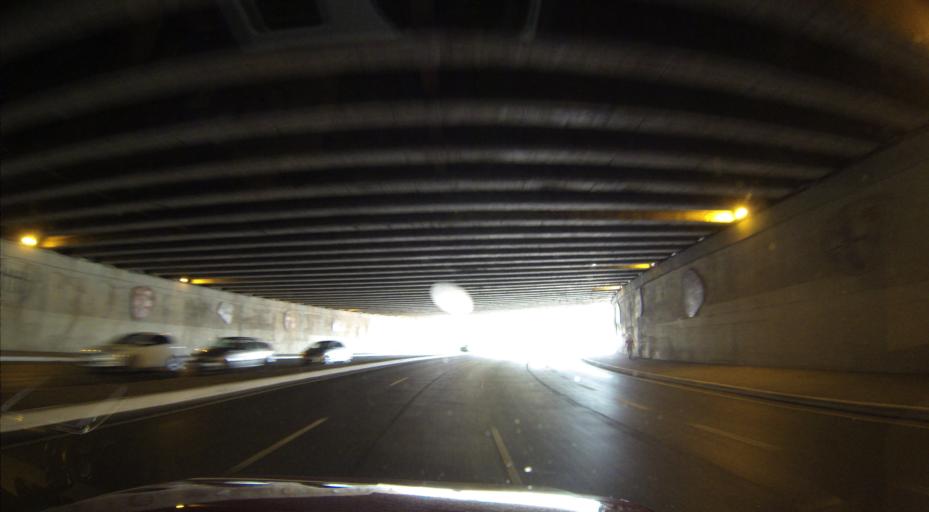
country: BR
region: Minas Gerais
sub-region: Belo Horizonte
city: Belo Horizonte
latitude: -19.8851
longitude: -43.9510
